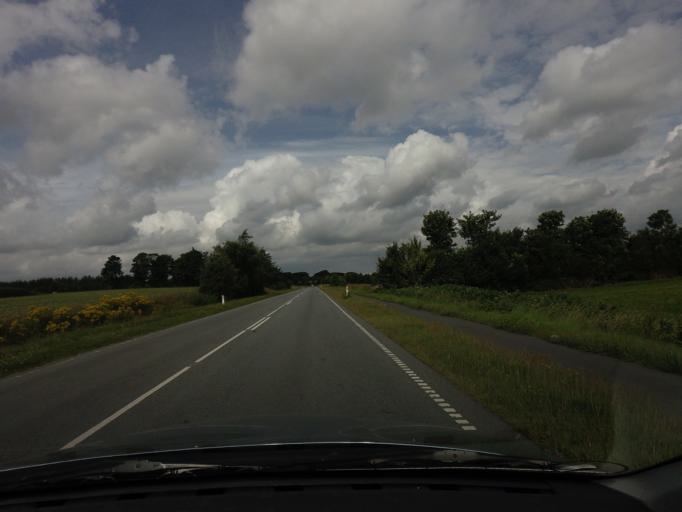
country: DK
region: North Denmark
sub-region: Hjorring Kommune
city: Tars
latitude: 57.3781
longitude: 10.1503
